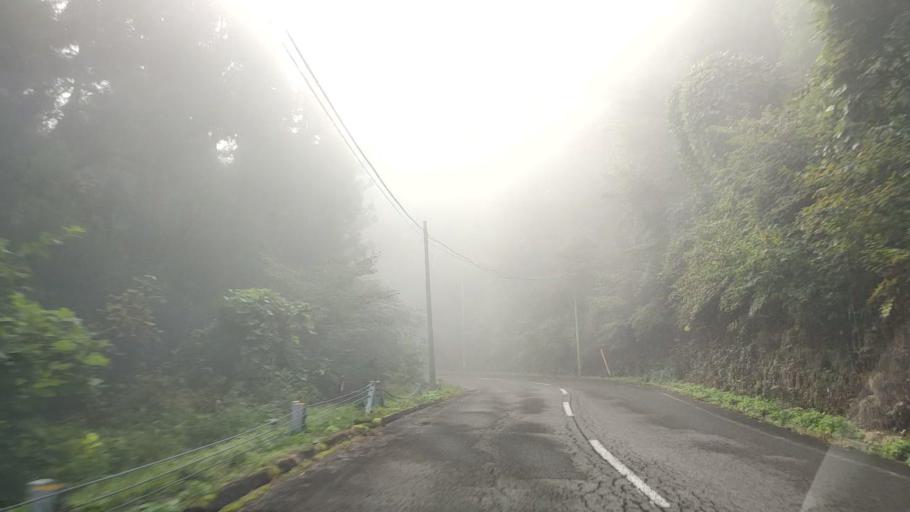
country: JP
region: Nagano
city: Iiyama
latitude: 36.8219
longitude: 138.4198
